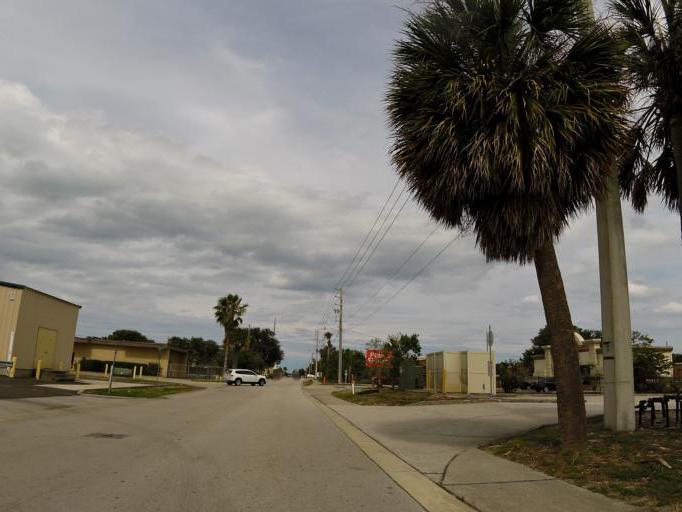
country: US
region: Florida
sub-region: Duval County
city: Jacksonville Beach
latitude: 30.2866
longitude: -81.4018
